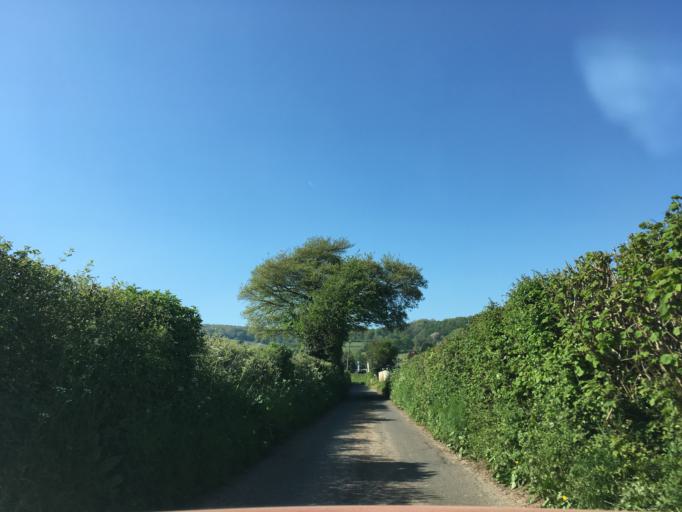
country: GB
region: Wales
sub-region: Newport
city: Llanvaches
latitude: 51.6233
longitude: -2.7967
